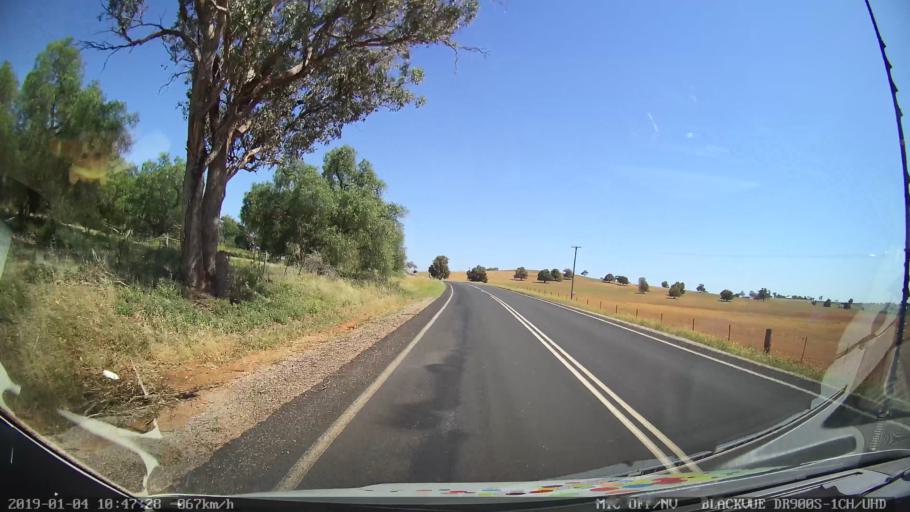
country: AU
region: New South Wales
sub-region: Cabonne
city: Molong
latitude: -33.2696
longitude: 148.7194
